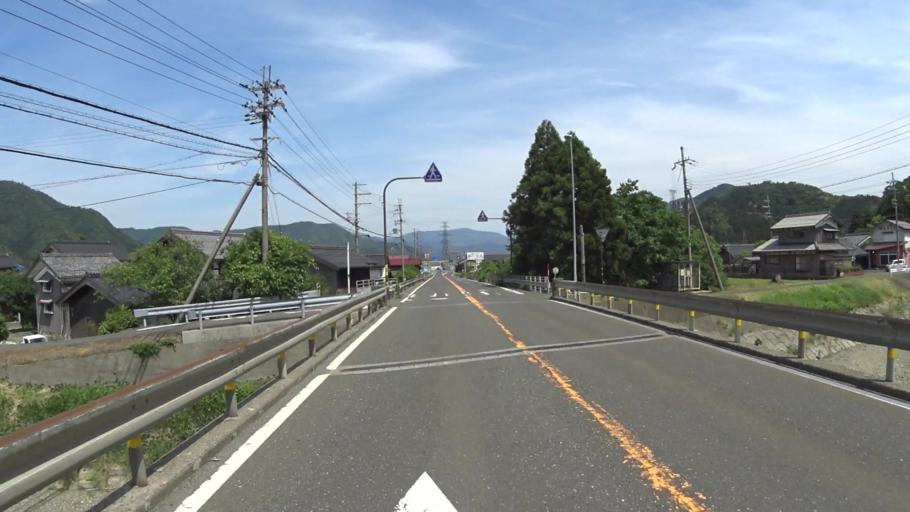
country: JP
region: Fukui
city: Obama
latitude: 35.4795
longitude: 135.7920
